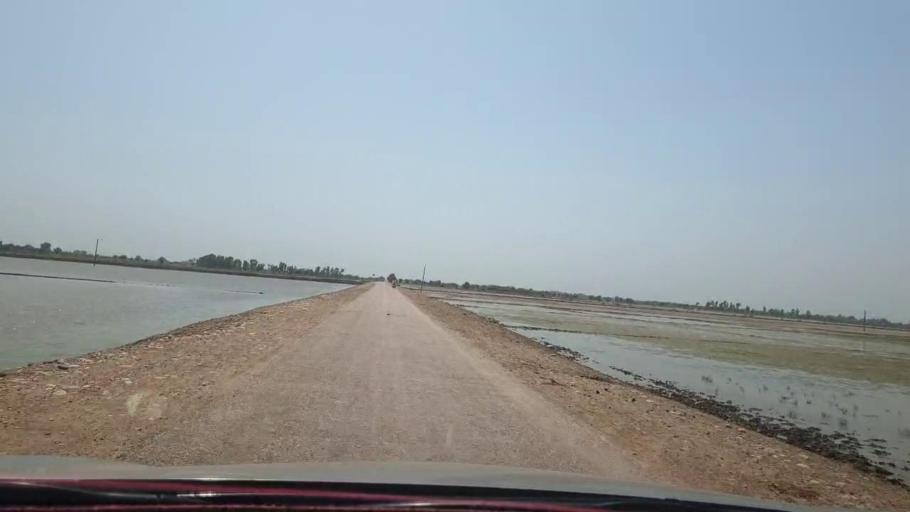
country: PK
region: Sindh
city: Warah
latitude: 27.5478
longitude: 67.7944
